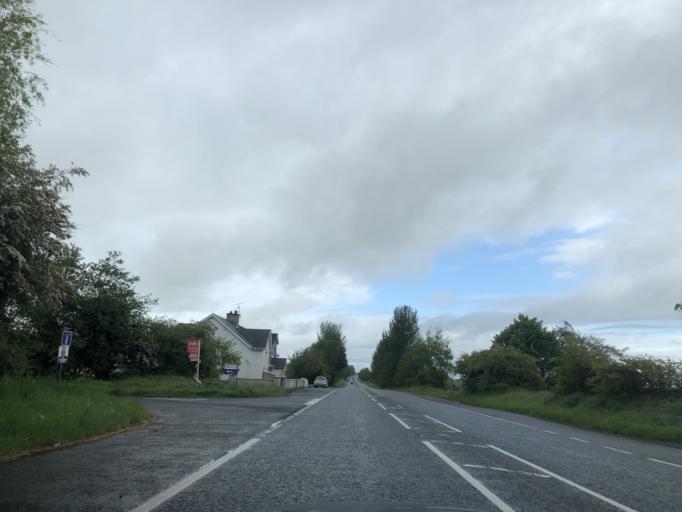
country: GB
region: Northern Ireland
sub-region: Ballymoney District
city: Ballymoney
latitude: 55.1147
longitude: -6.5467
